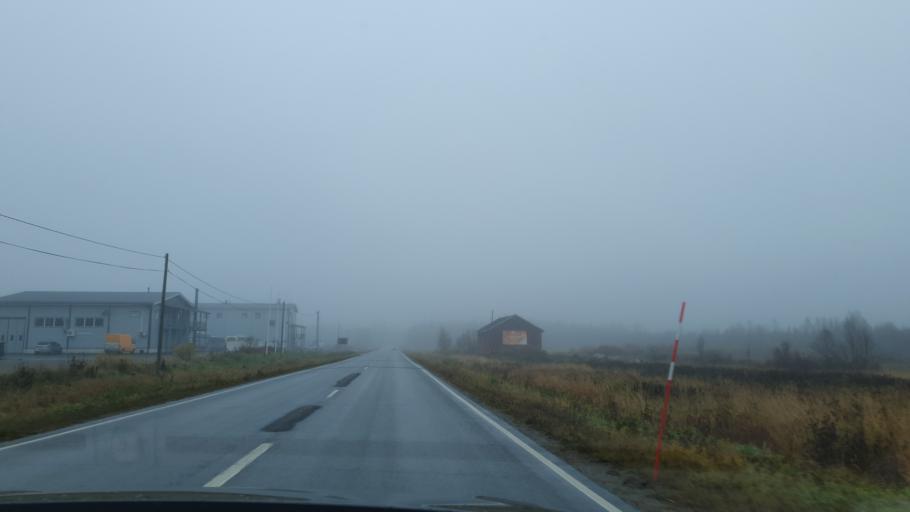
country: FI
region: Lapland
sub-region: Tunturi-Lappi
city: Kittilae
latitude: 67.6675
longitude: 24.8632
